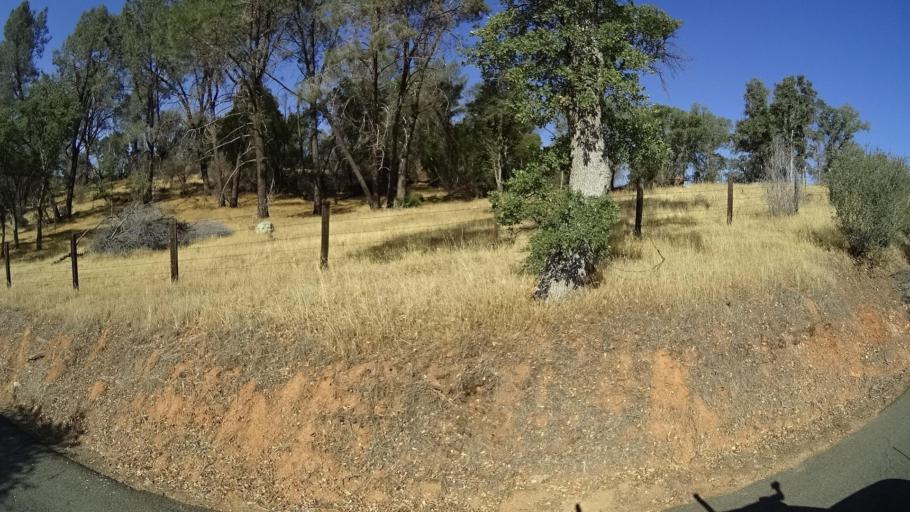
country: US
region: California
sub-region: Mariposa County
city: Mariposa
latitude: 37.5855
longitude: -120.1786
